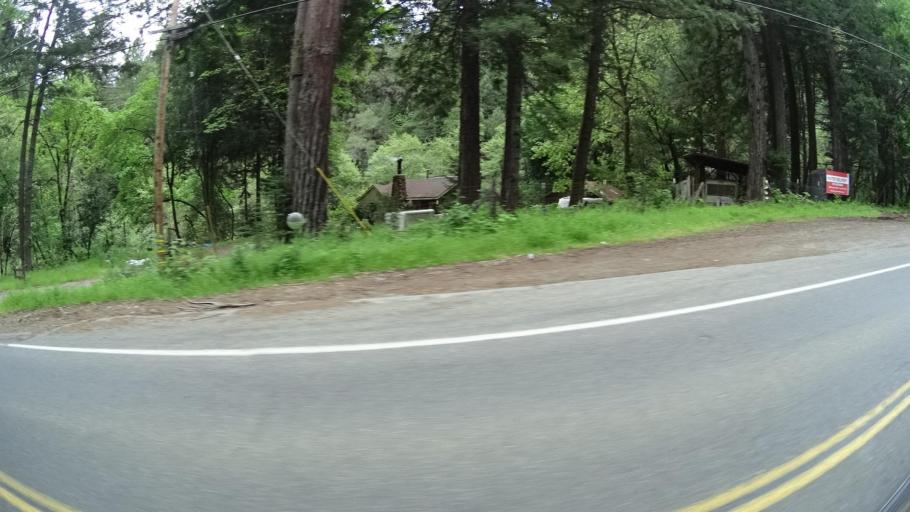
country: US
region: California
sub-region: Humboldt County
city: Redway
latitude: 40.1263
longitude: -123.8482
